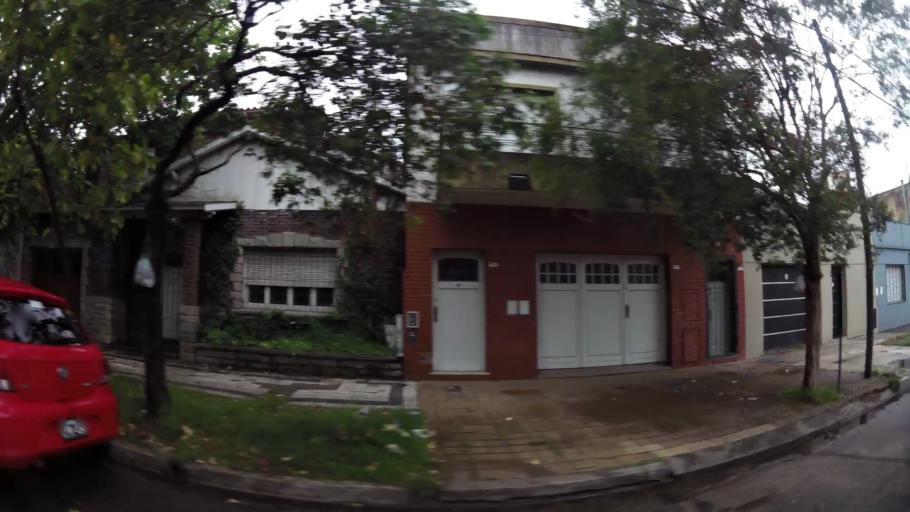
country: AR
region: Buenos Aires
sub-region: Partido de Lomas de Zamora
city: Lomas de Zamora
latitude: -34.7475
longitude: -58.3924
